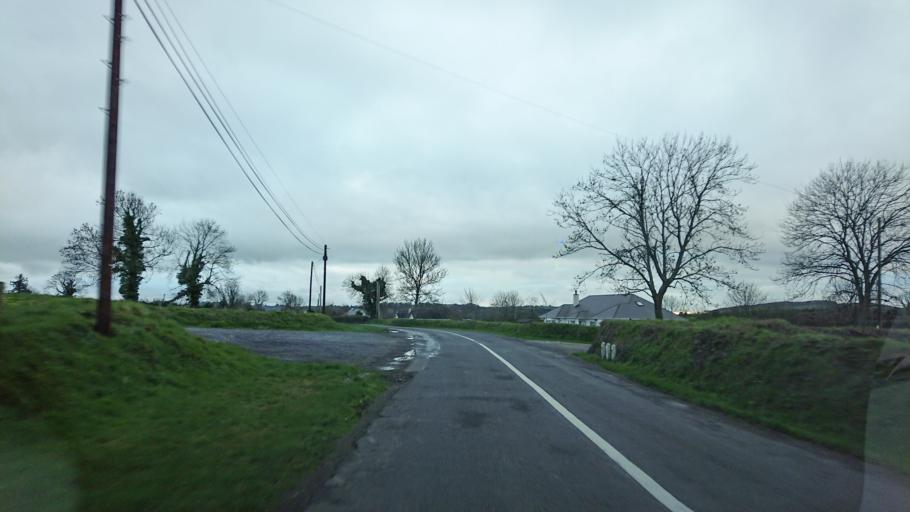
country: IE
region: Munster
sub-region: Waterford
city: Portlaw
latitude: 52.1839
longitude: -7.4087
